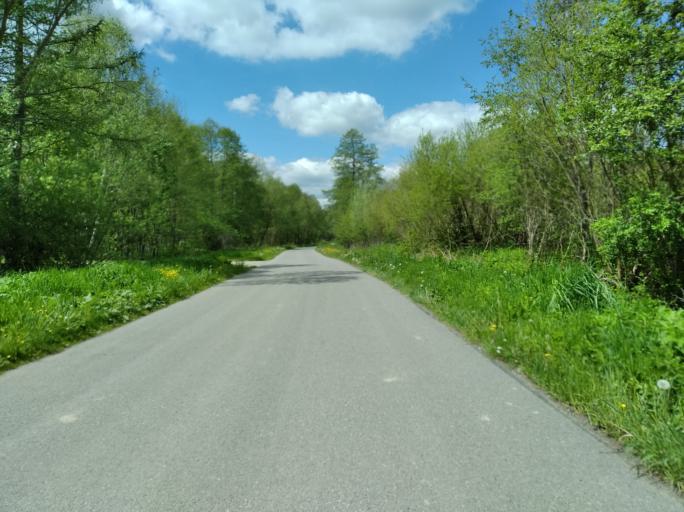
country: PL
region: Subcarpathian Voivodeship
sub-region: Powiat ropczycko-sedziszowski
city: Wielopole Skrzynskie
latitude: 49.9337
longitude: 21.6386
